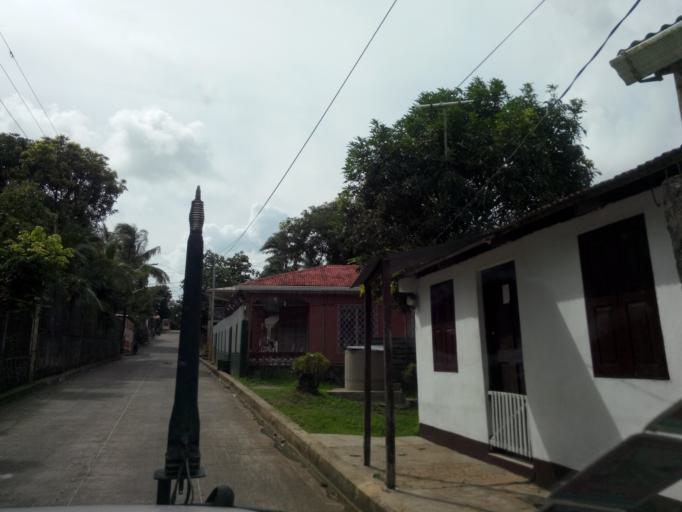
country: NI
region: Atlantico Sur
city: Bluefields
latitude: 12.0001
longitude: -83.7650
